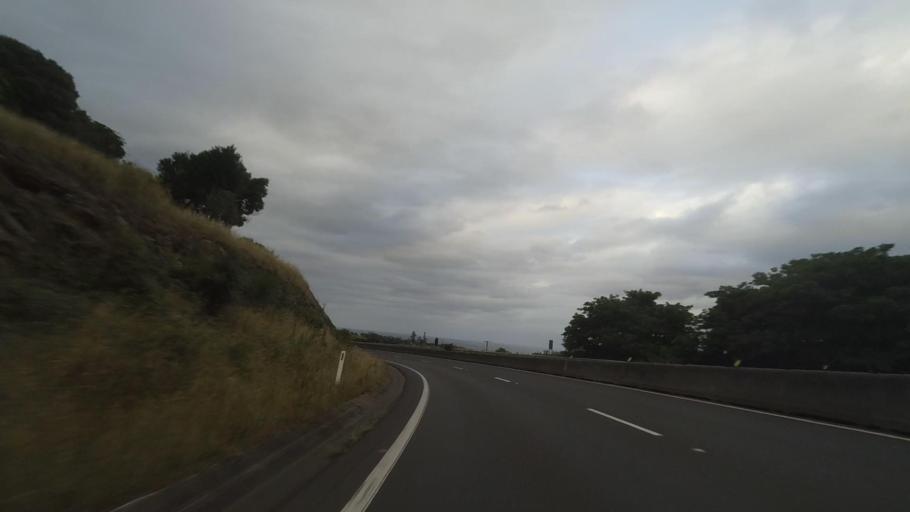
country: AU
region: New South Wales
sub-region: Kiama
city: Kiama
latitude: -34.7033
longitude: 150.8379
